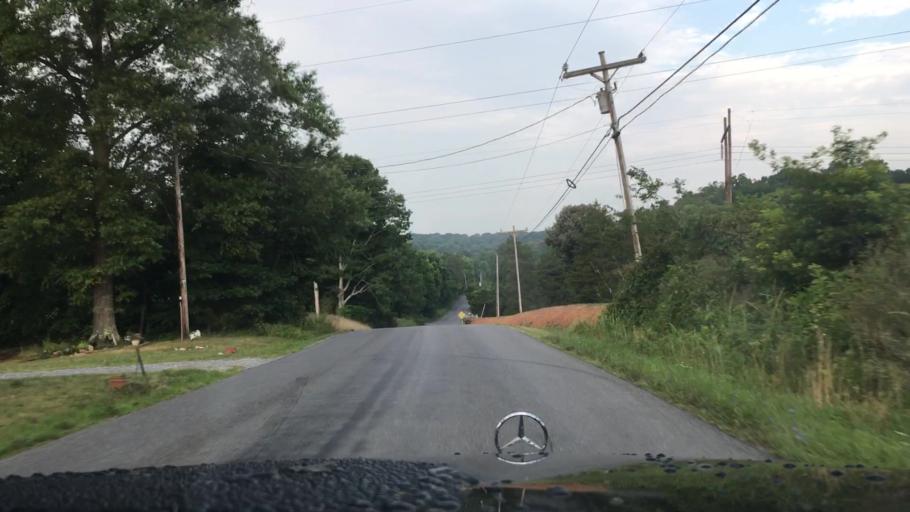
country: US
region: Virginia
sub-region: Campbell County
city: Altavista
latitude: 37.1468
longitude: -79.2790
